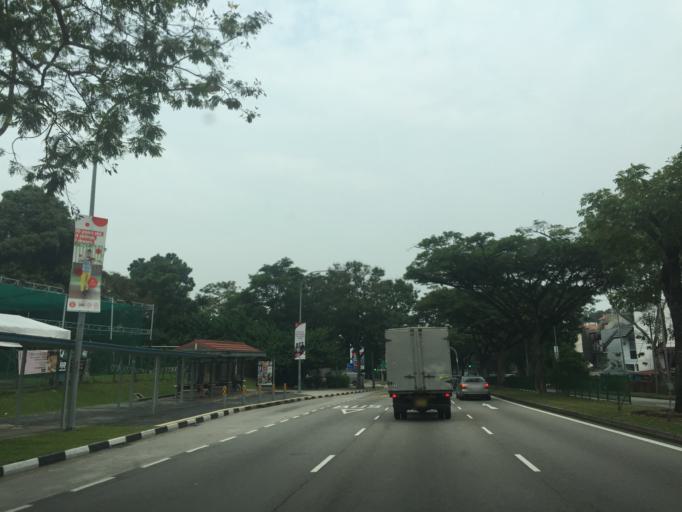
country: SG
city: Singapore
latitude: 1.3740
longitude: 103.8286
